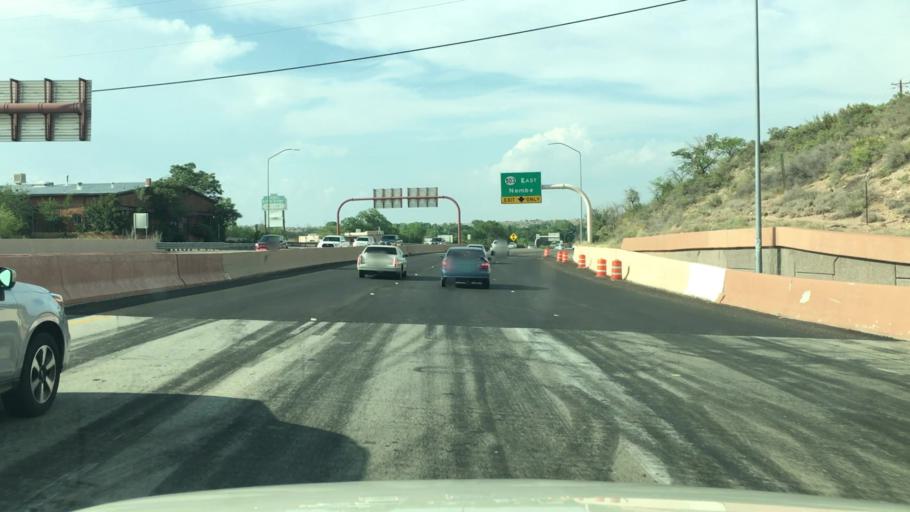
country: US
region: New Mexico
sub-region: Santa Fe County
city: Pojoaque
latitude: 35.8928
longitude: -106.0229
